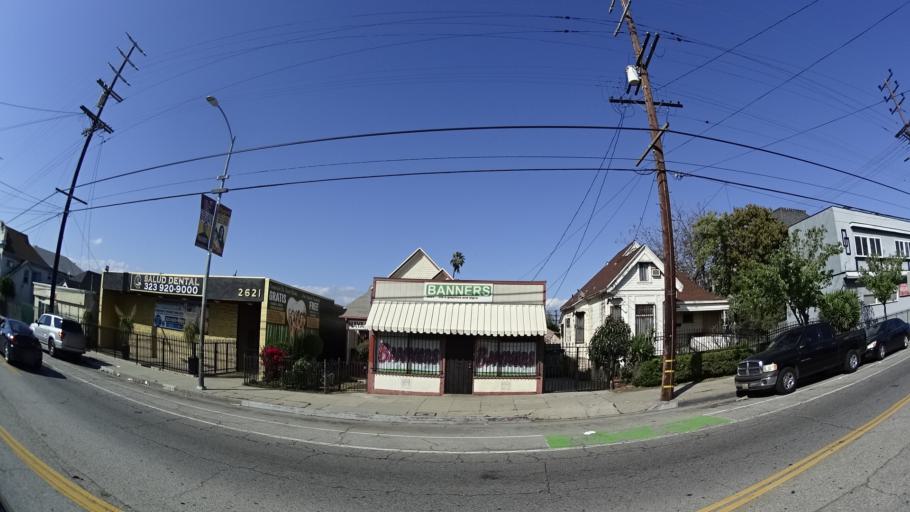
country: US
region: California
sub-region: Los Angeles County
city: Boyle Heights
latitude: 34.0422
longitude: -118.2065
